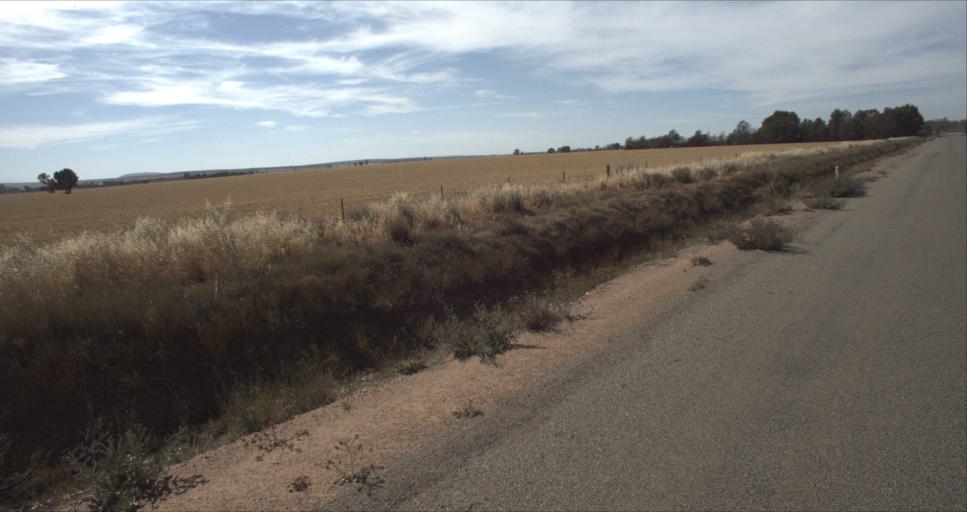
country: AU
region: New South Wales
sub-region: Leeton
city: Leeton
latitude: -34.5687
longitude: 146.4731
